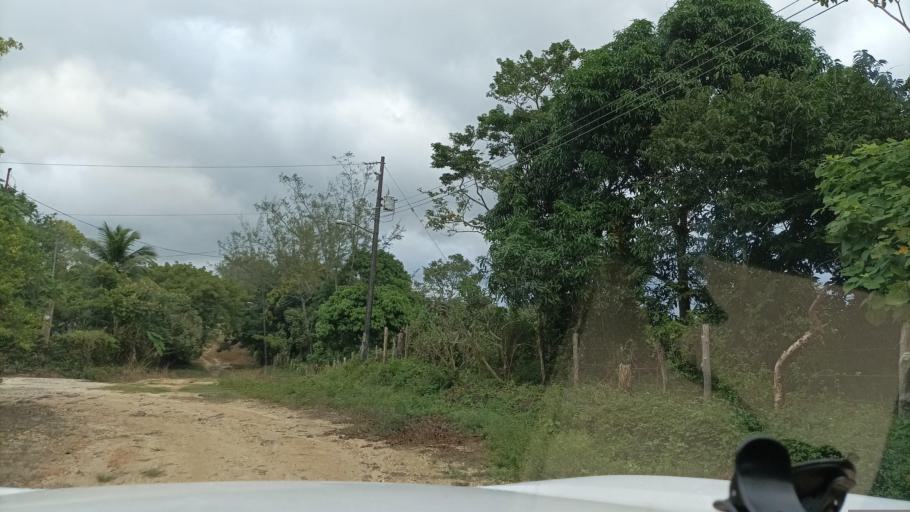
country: MX
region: Veracruz
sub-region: Moloacan
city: Cuichapa
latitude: 17.9212
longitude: -94.3663
